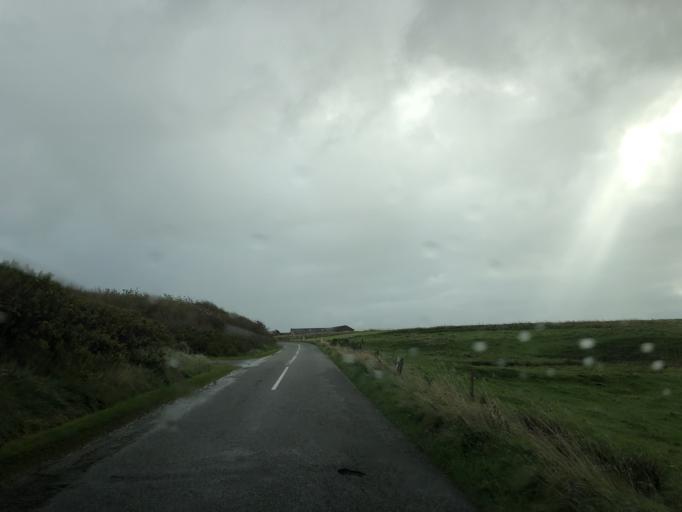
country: DK
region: Central Jutland
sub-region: Lemvig Kommune
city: Harboore
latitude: 56.5369
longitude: 8.1355
